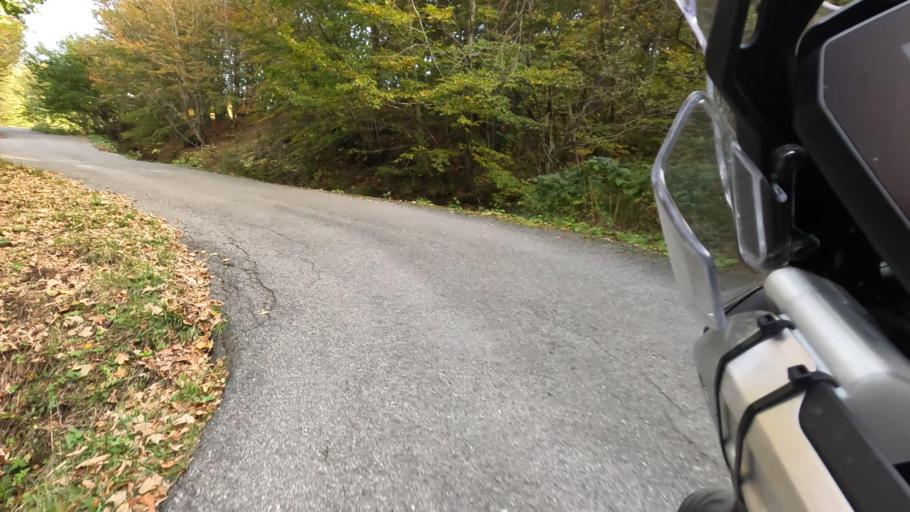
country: IT
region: Liguria
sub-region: Provincia di Genova
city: Sciarborasca
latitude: 44.4342
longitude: 8.5847
